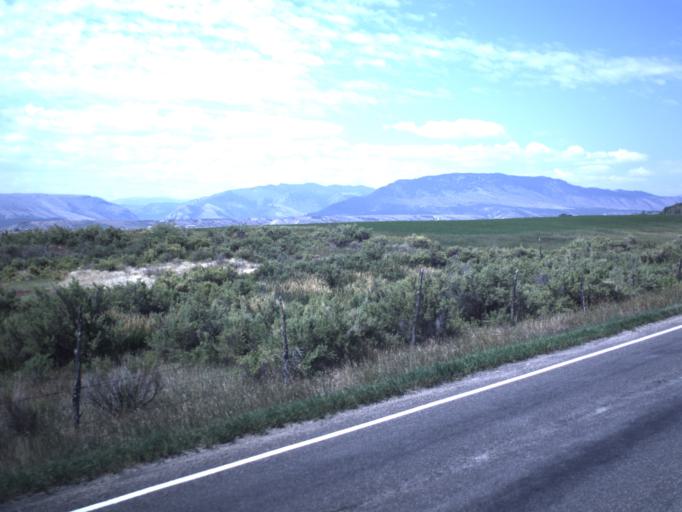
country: US
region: Utah
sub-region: Daggett County
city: Manila
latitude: 40.9886
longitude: -109.7033
